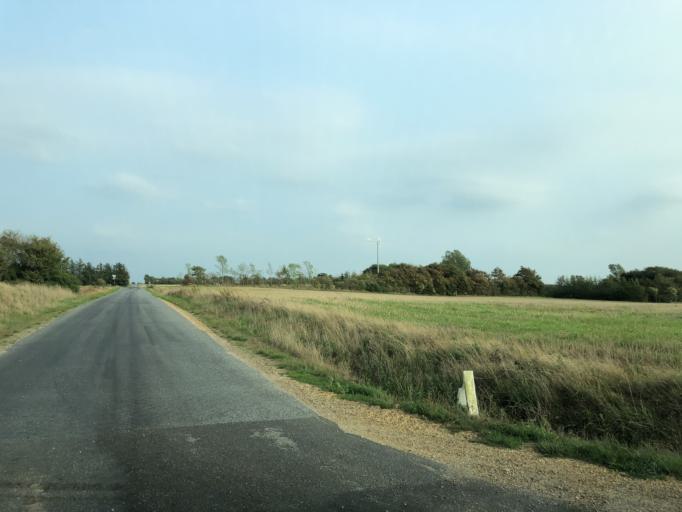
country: DK
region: Central Jutland
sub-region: Ringkobing-Skjern Kommune
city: Videbaek
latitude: 56.1236
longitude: 8.6513
